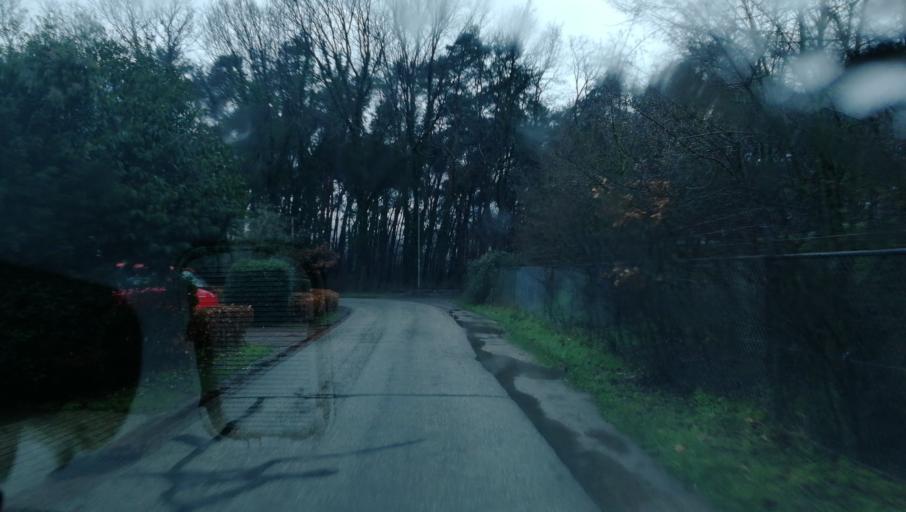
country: NL
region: Limburg
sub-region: Gemeente Venlo
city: Tegelen
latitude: 51.3487
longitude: 6.1003
